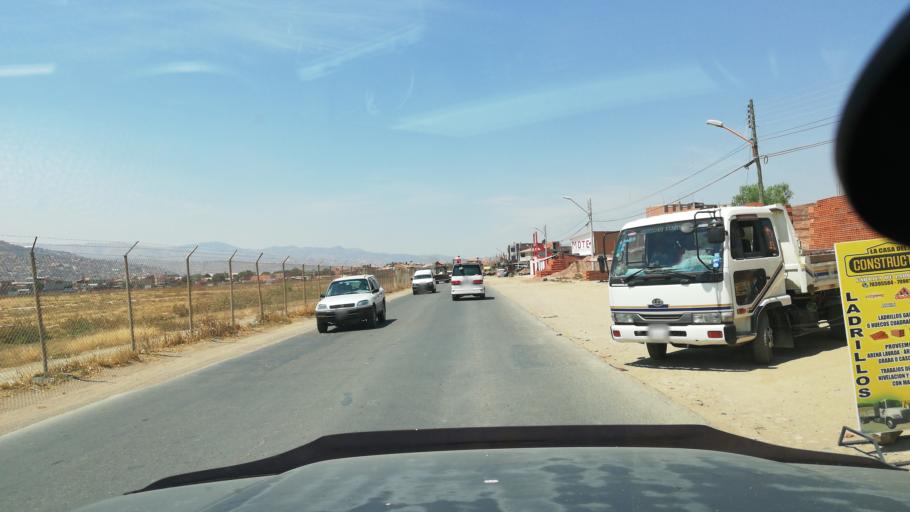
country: BO
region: Cochabamba
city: Cochabamba
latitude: -17.4322
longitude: -66.1667
